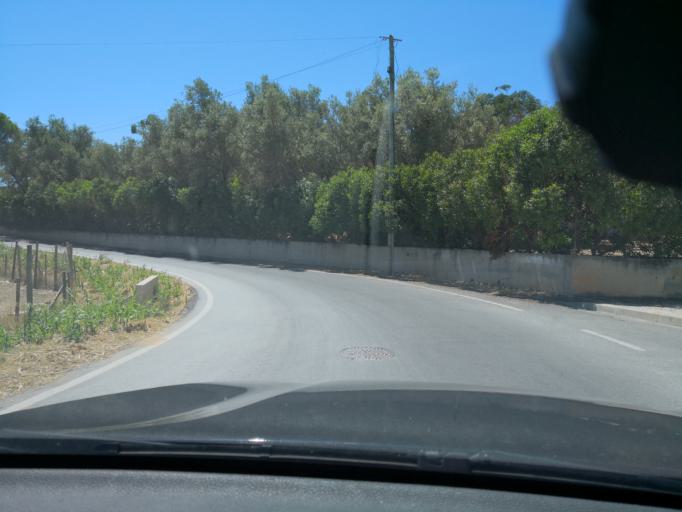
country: PT
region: Faro
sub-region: Loule
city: Quarteira
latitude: 37.0680
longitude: -8.0843
